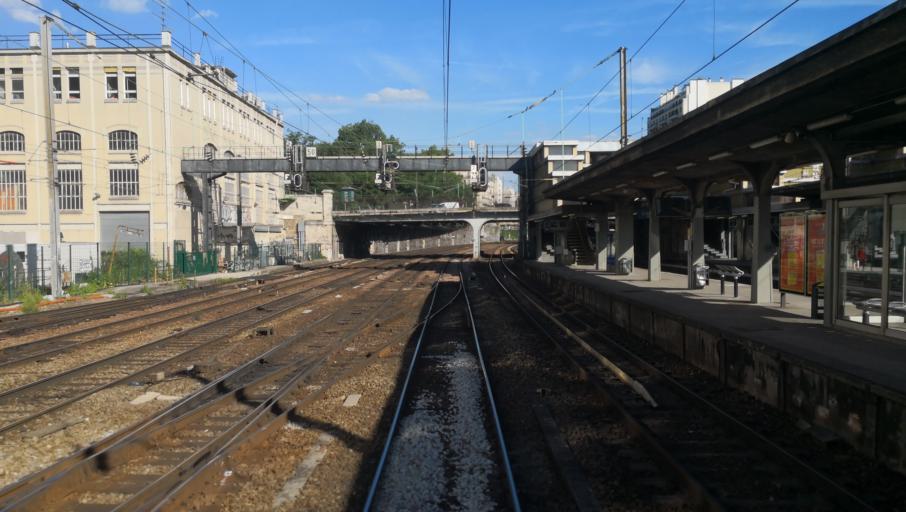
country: FR
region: Ile-de-France
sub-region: Paris
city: Saint-Ouen
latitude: 48.8825
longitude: 2.3334
